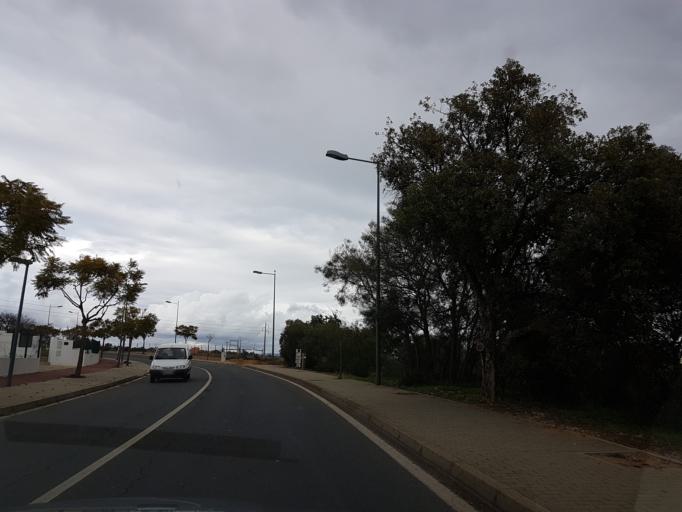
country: PT
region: Faro
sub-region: Albufeira
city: Ferreiras
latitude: 37.1107
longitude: -8.2287
